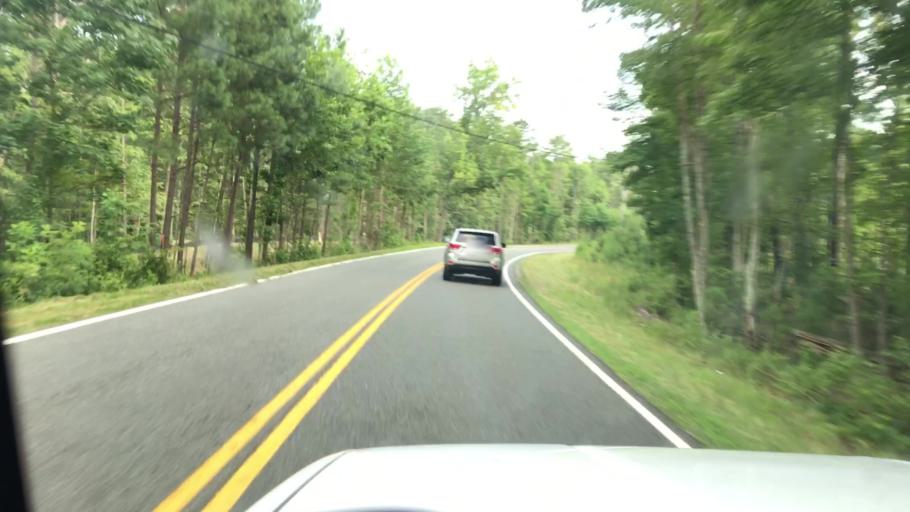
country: US
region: Virginia
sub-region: Henrico County
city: Short Pump
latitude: 37.6416
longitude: -77.6790
